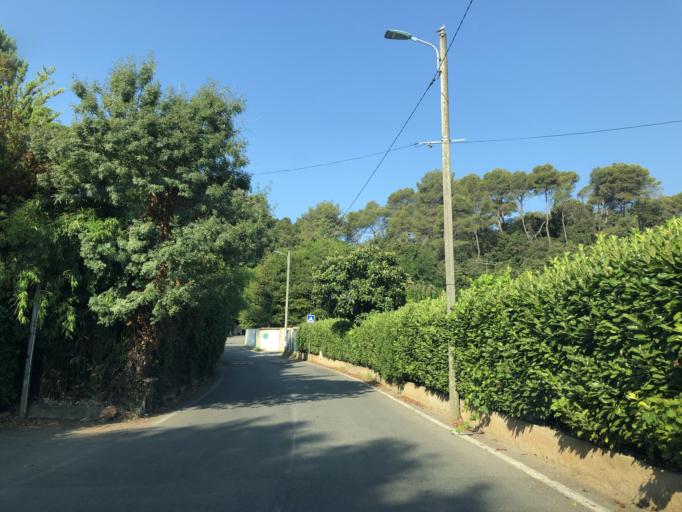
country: FR
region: Provence-Alpes-Cote d'Azur
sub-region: Departement des Alpes-Maritimes
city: Biot
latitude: 43.6229
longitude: 7.0966
